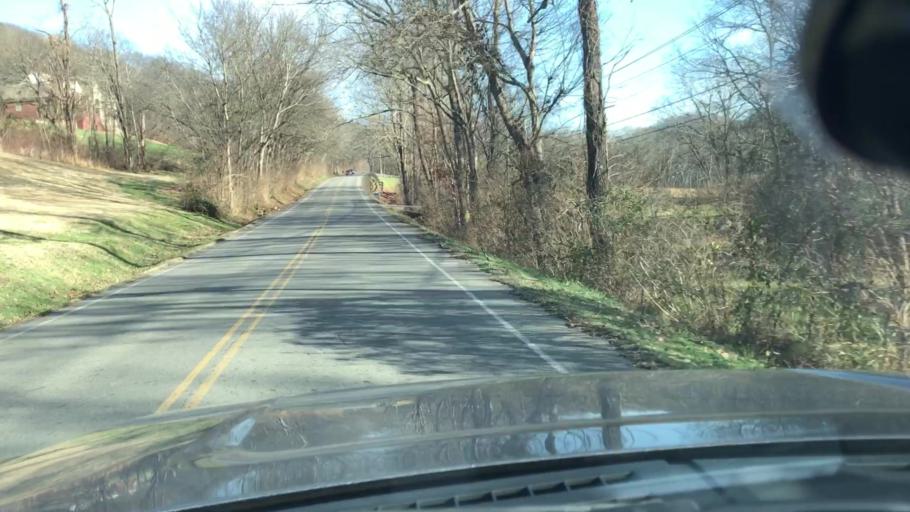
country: US
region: Tennessee
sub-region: Williamson County
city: Brentwood Estates
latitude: 36.0025
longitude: -86.8379
